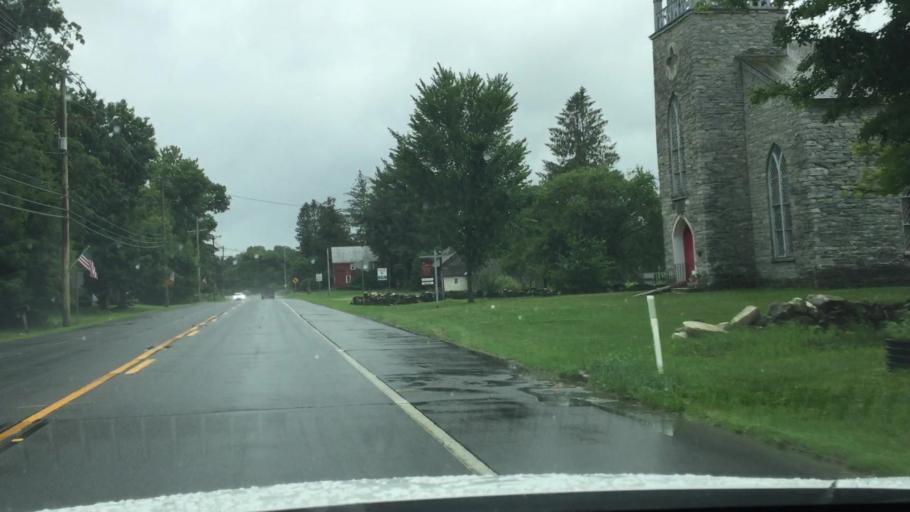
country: US
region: Massachusetts
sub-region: Berkshire County
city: Lanesborough
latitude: 42.5354
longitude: -73.2295
